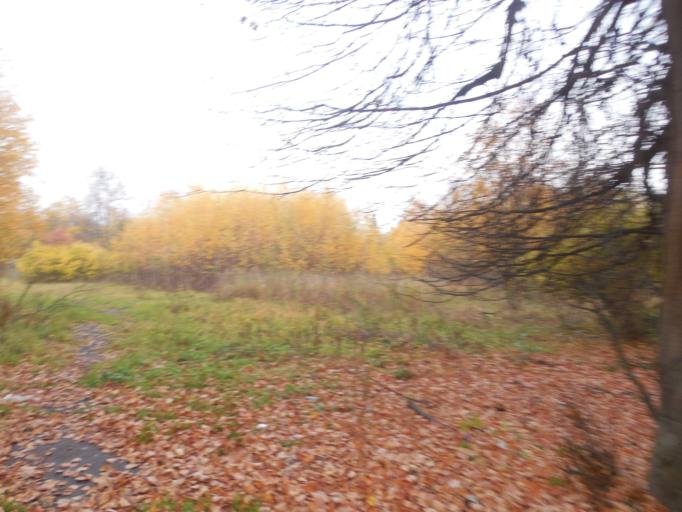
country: RU
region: Moskovskaya
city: Shcherbinka
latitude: 55.4956
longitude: 37.5883
